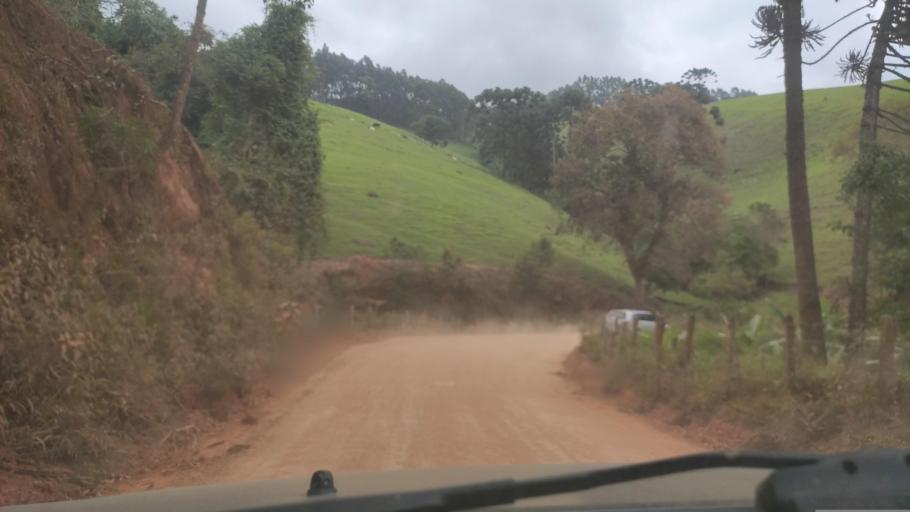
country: BR
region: Minas Gerais
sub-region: Paraisopolis
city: Paraisopolis
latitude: -22.6613
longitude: -45.8823
